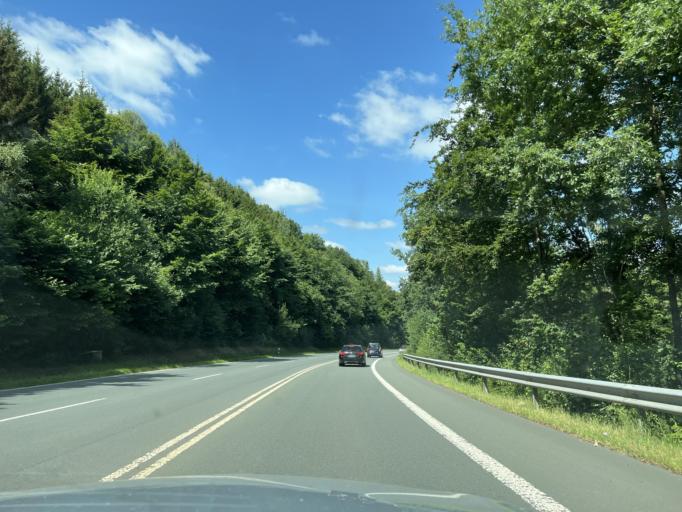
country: DE
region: North Rhine-Westphalia
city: Freudenberg
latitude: 50.9109
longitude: 7.8953
